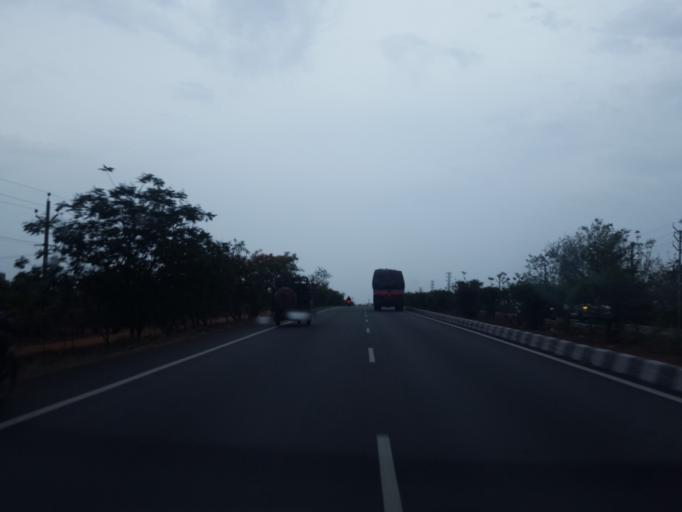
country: IN
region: Telangana
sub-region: Mahbubnagar
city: Farrukhnagar
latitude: 17.1202
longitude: 78.2717
